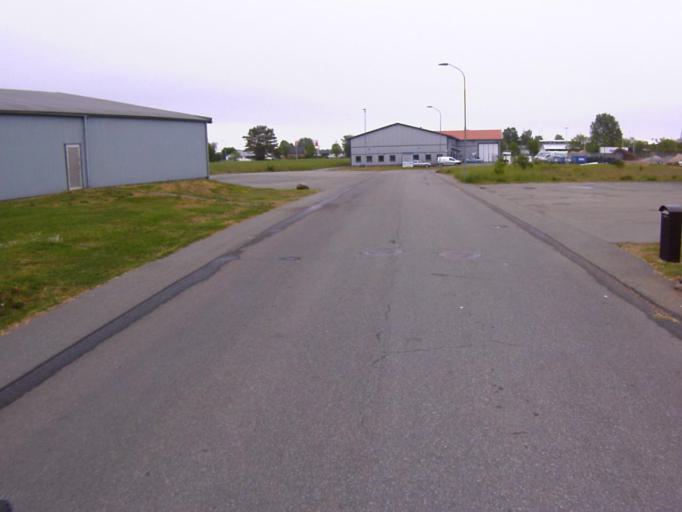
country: SE
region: Skane
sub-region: Kristianstads Kommun
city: Ahus
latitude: 55.9311
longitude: 14.2861
